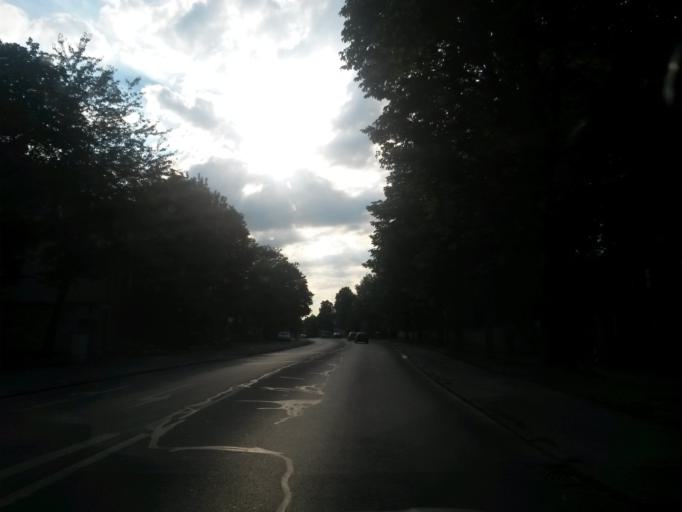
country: DE
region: Bavaria
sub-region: Upper Bavaria
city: Neubiberg
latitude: 48.0992
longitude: 11.6348
